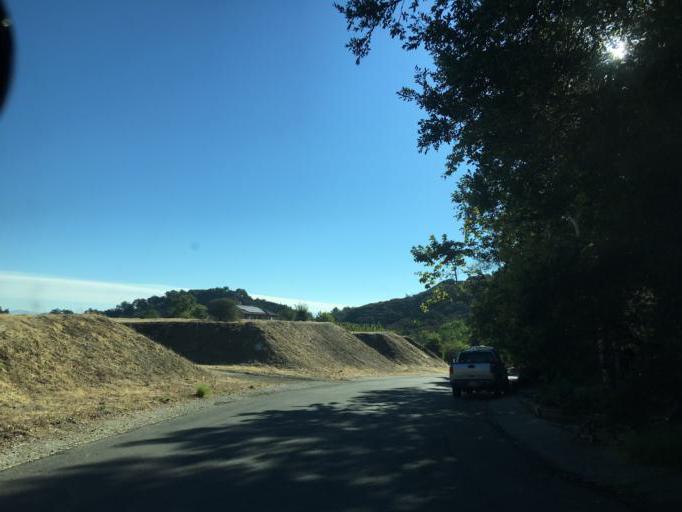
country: US
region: California
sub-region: Los Angeles County
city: Westlake Village
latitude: 34.0913
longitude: -118.8080
